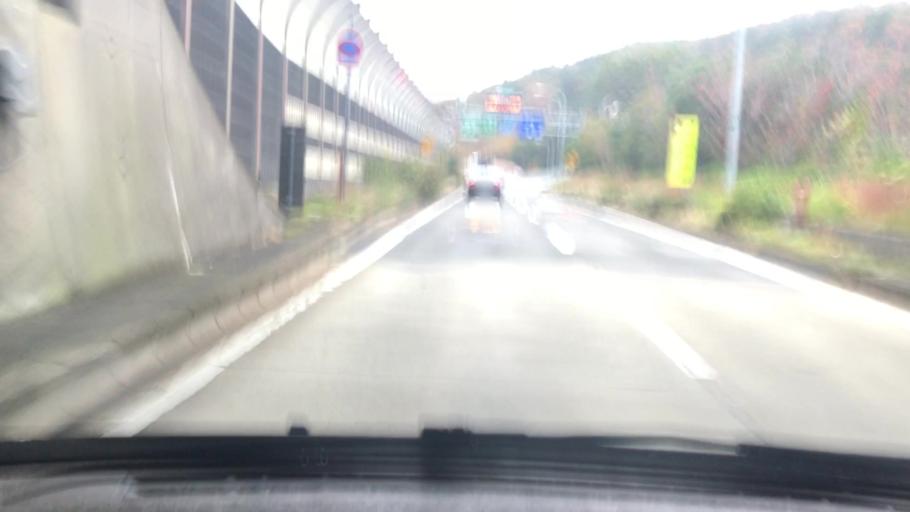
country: JP
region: Hyogo
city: Kobe
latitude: 34.7561
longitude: 135.1610
